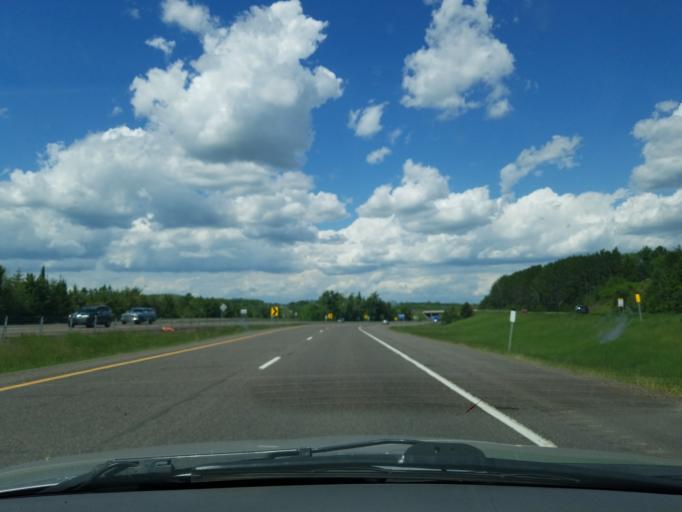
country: US
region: Minnesota
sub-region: Carlton County
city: Cloquet
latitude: 46.6863
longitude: -92.4591
